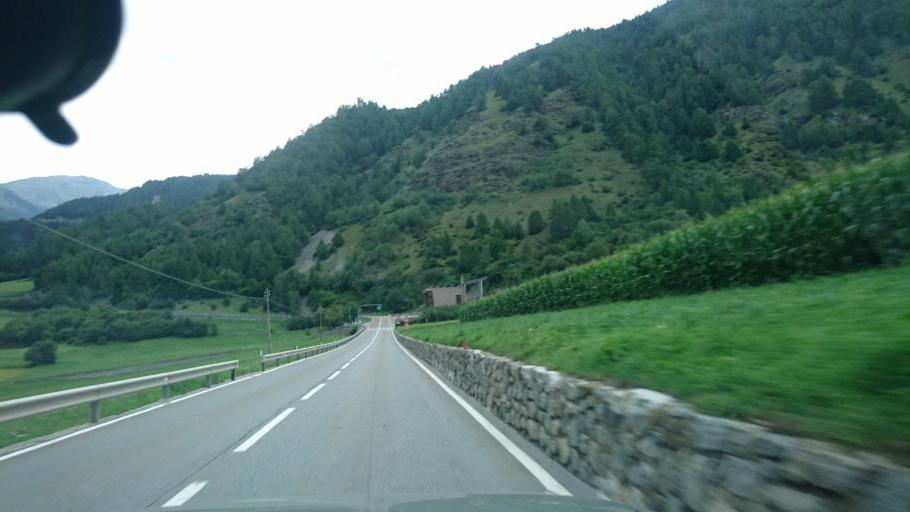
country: IT
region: Trentino-Alto Adige
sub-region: Bolzano
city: Tubre
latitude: 46.6542
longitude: 10.4797
